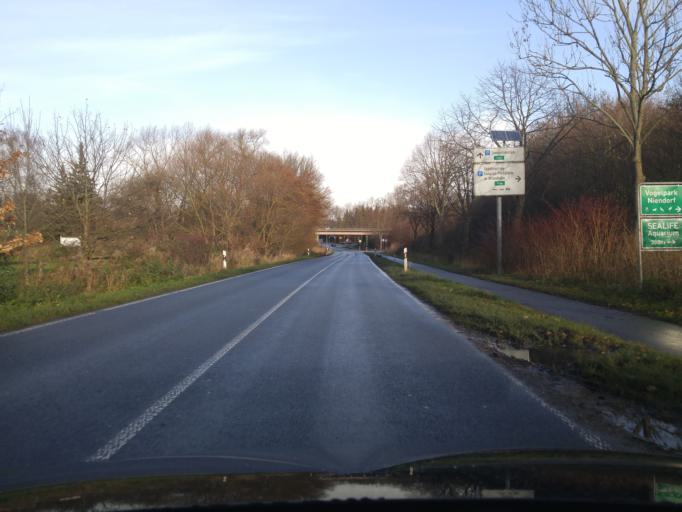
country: DE
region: Schleswig-Holstein
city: Timmendorfer Strand
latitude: 53.9907
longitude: 10.7727
